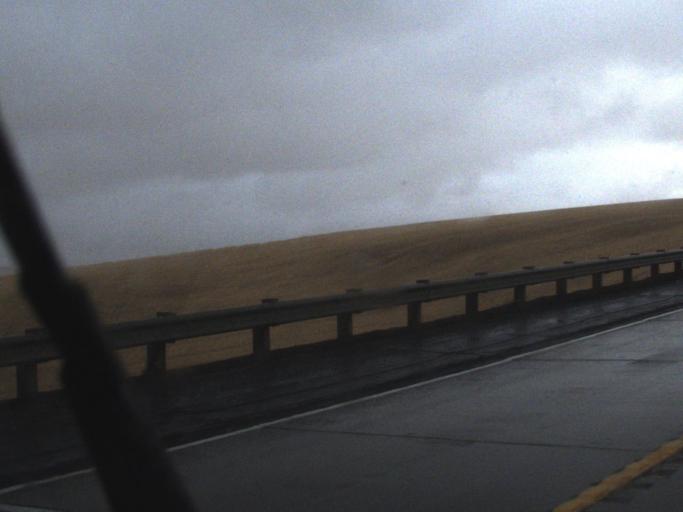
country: US
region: Washington
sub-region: Whitman County
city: Colfax
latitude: 47.0839
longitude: -117.3817
